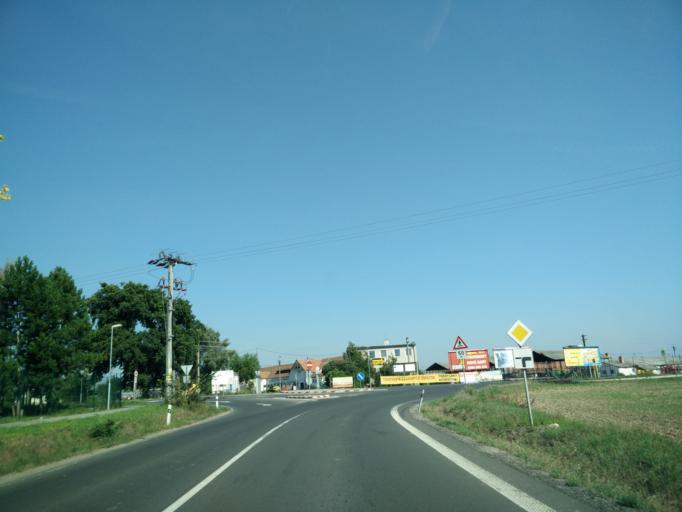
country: SK
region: Nitriansky
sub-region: Okres Nitra
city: Nitra
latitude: 48.3726
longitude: 18.0412
